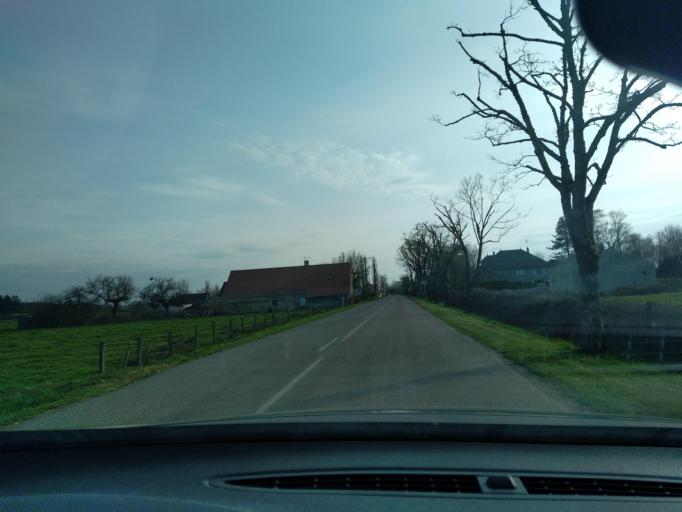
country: FR
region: Franche-Comte
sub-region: Departement du Jura
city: Chaussin
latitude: 46.9937
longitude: 5.4682
